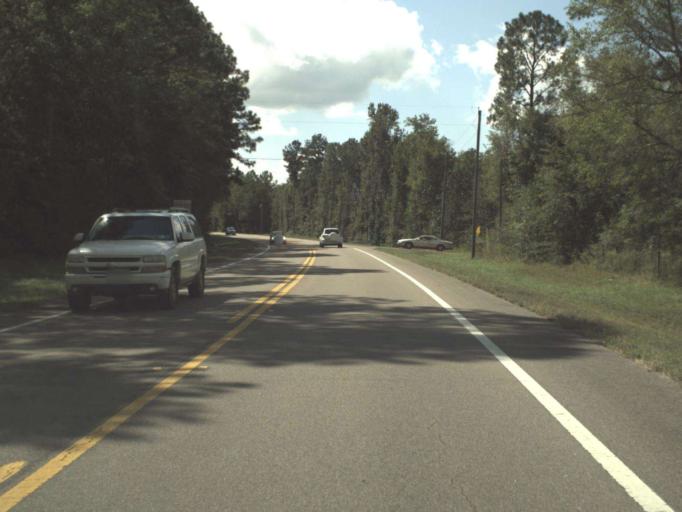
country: US
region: Florida
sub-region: Walton County
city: Freeport
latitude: 30.4785
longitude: -85.9607
